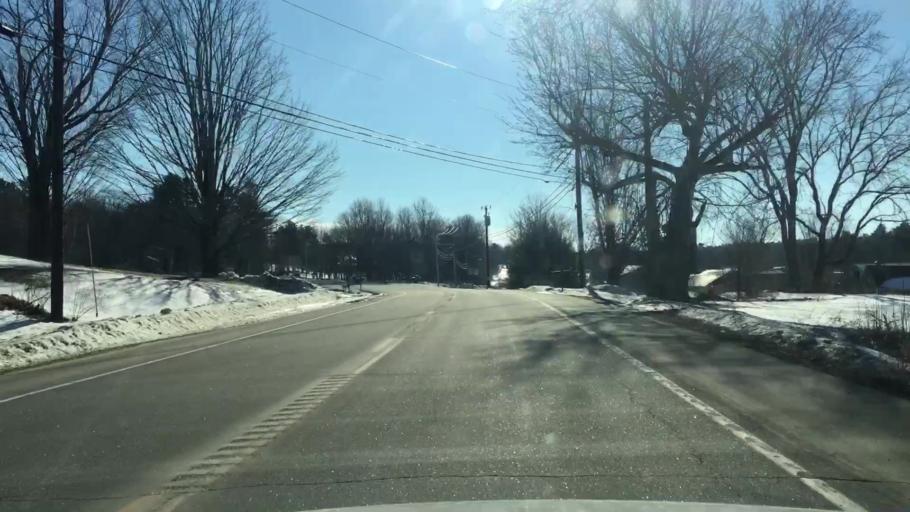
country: US
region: Maine
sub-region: Cumberland County
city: North Windham
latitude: 43.8108
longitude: -70.4023
